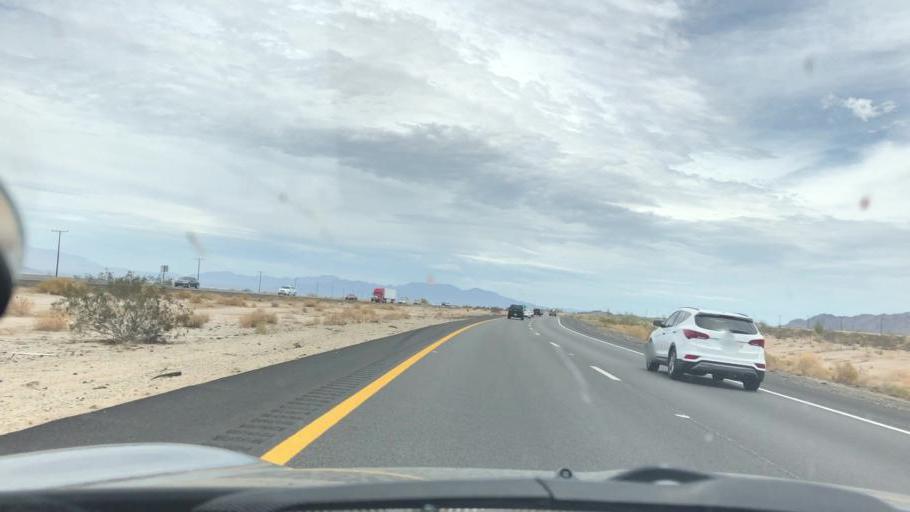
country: US
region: California
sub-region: Imperial County
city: Niland
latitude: 33.6999
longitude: -115.4632
